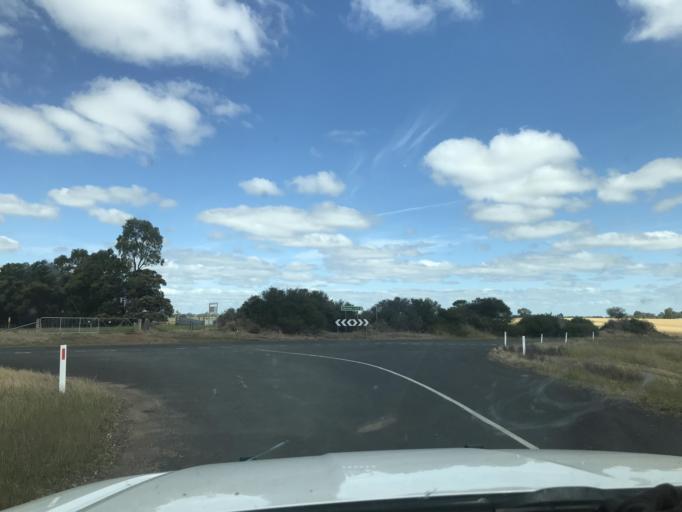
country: AU
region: South Australia
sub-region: Naracoorte and Lucindale
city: Naracoorte
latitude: -36.9979
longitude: 141.2961
